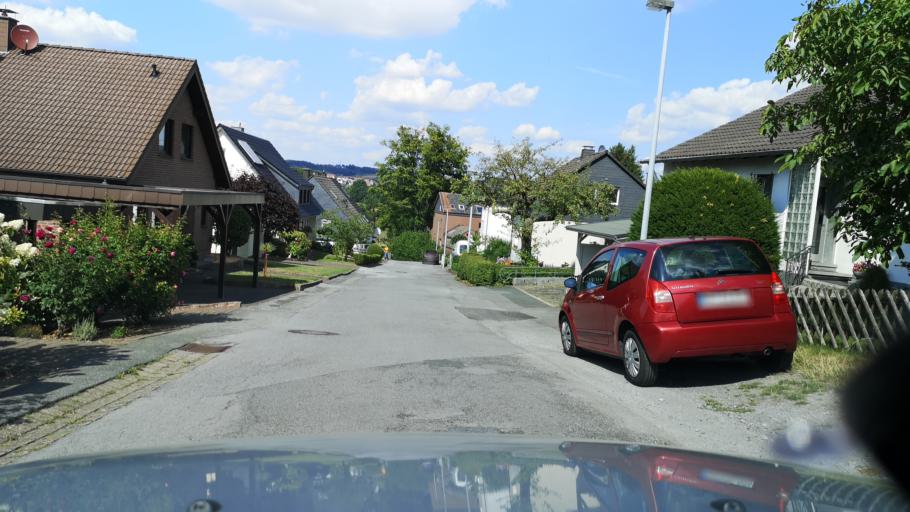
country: DE
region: North Rhine-Westphalia
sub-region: Regierungsbezirk Arnsberg
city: Frondenberg
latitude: 51.4578
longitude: 7.7660
